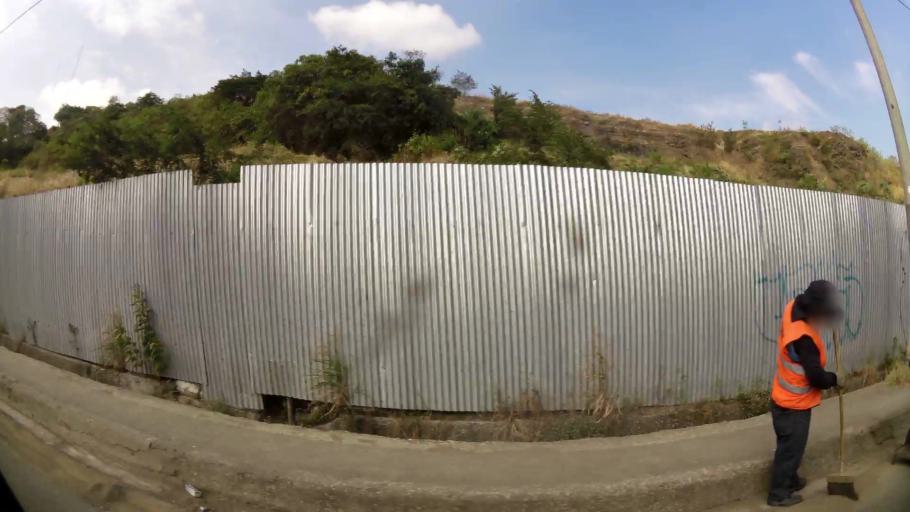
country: EC
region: Guayas
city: Guayaquil
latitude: -2.1792
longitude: -79.9070
